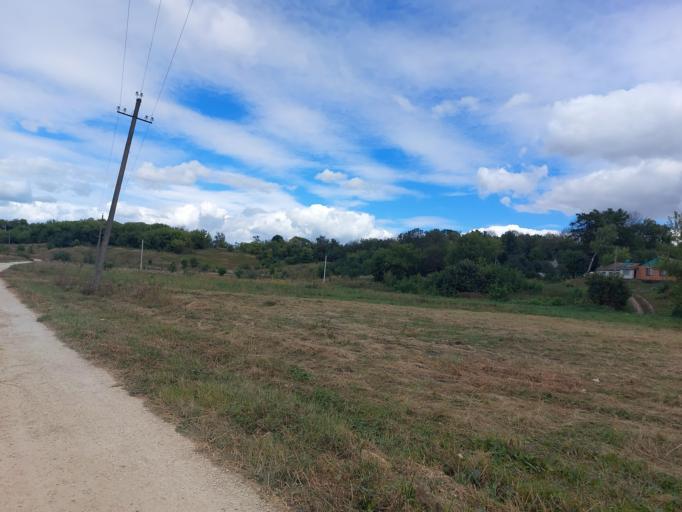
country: RU
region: Lipetsk
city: Terbuny
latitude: 52.2673
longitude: 38.2050
